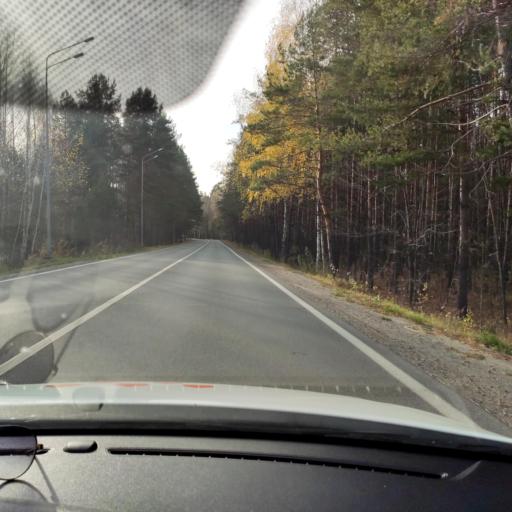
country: RU
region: Tatarstan
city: Verkhniy Uslon
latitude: 55.6361
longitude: 49.0214
